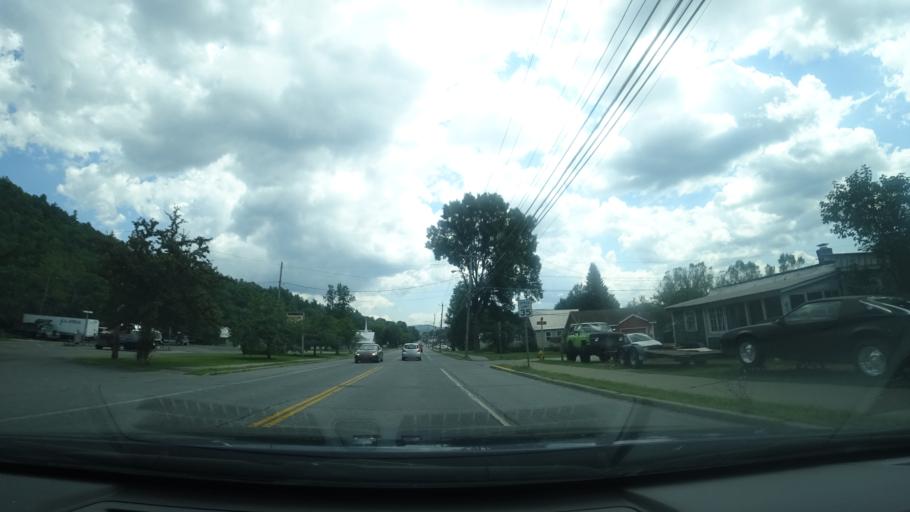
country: US
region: New York
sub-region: Warren County
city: Warrensburg
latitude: 43.5032
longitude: -73.7857
